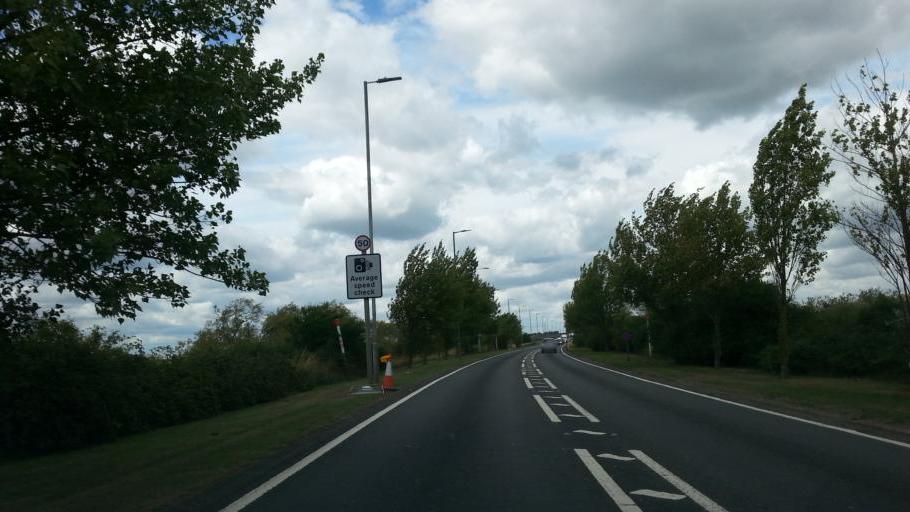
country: GB
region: England
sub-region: Essex
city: South Benfleet
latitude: 51.5424
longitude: 0.5487
